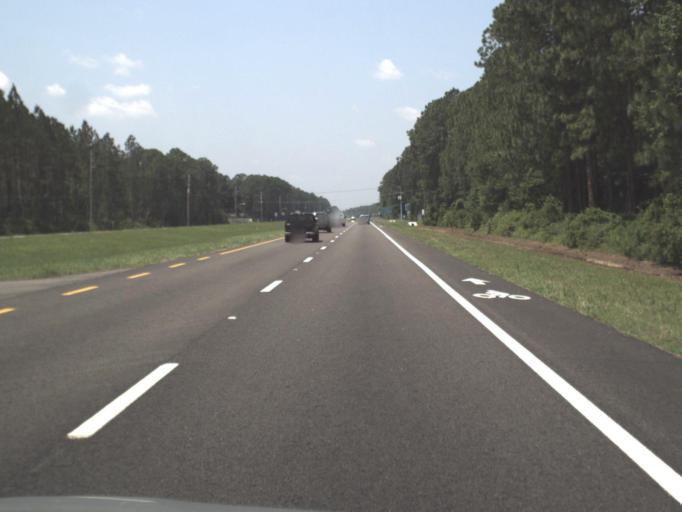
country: US
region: Florida
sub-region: Duval County
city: Baldwin
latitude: 30.2522
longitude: -81.8802
